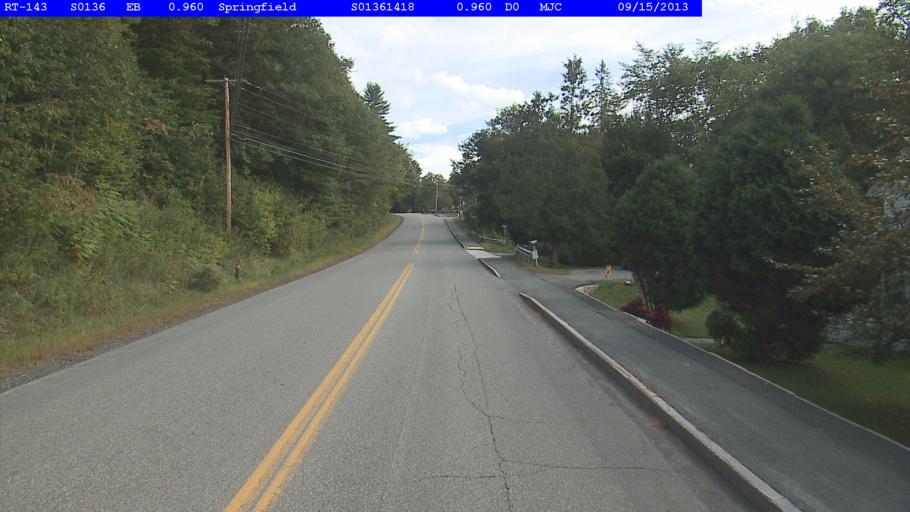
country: US
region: Vermont
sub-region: Windsor County
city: Springfield
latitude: 43.2935
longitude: -72.4674
